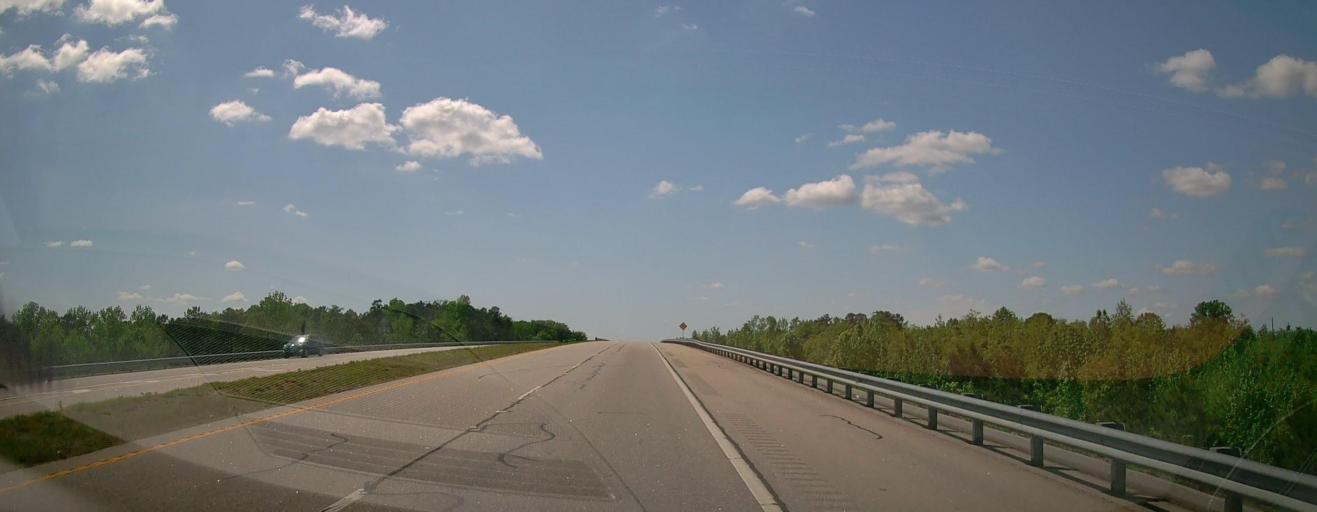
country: US
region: Georgia
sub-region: Putnam County
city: Eatonton
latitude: 33.2739
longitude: -83.3633
